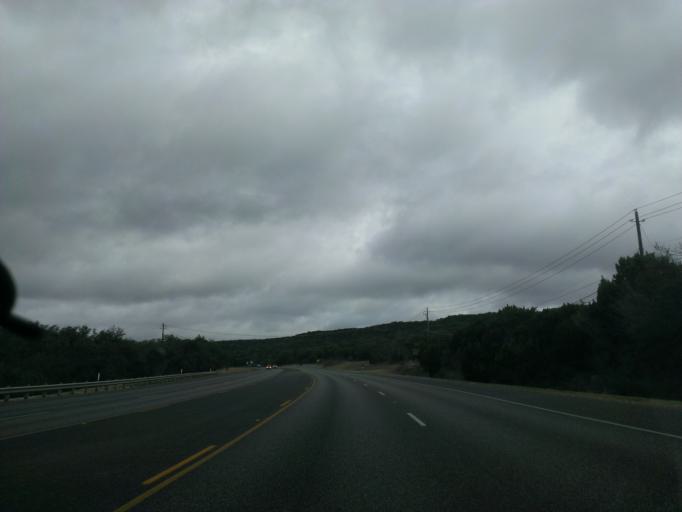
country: US
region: Texas
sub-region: Williamson County
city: Jollyville
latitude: 30.3791
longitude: -97.8067
